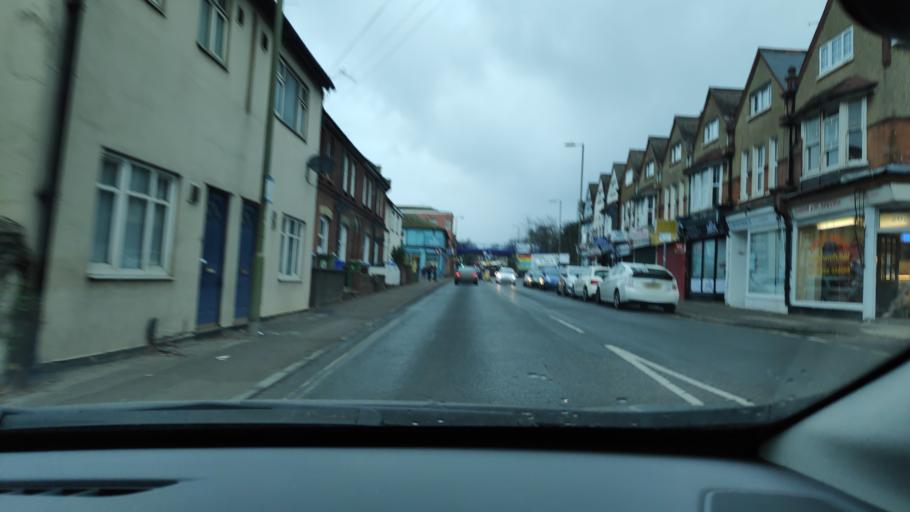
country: GB
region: England
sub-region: Hampshire
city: Aldershot
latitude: 51.2463
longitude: -0.7552
